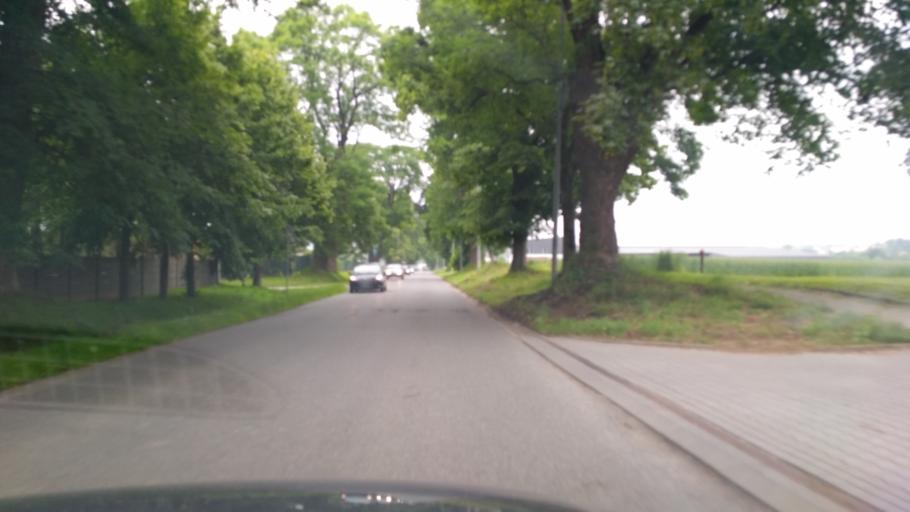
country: PL
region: Subcarpathian Voivodeship
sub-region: Powiat ropczycko-sedziszowski
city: Sedziszow Malopolski
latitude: 50.0578
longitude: 21.6896
